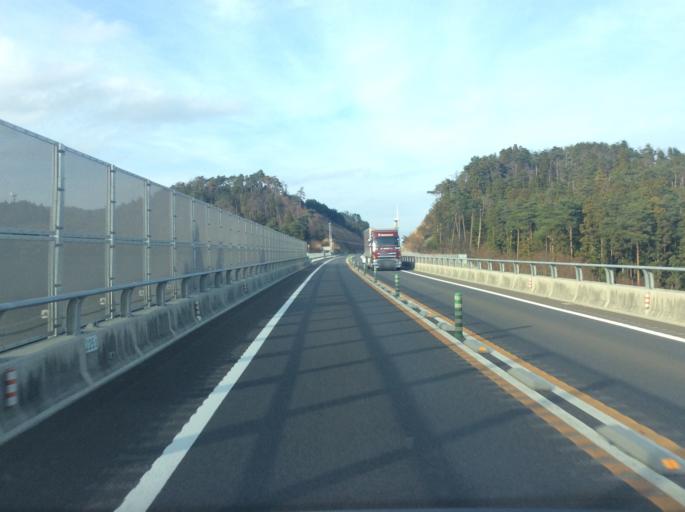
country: JP
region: Fukushima
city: Namie
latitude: 37.4344
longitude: 140.9589
